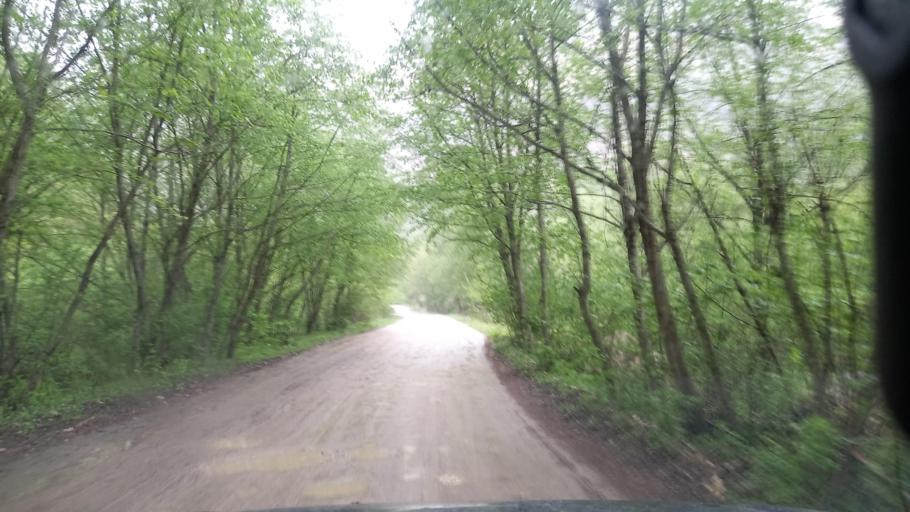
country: RU
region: Kabardino-Balkariya
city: Gundelen
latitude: 43.5909
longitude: 43.1276
